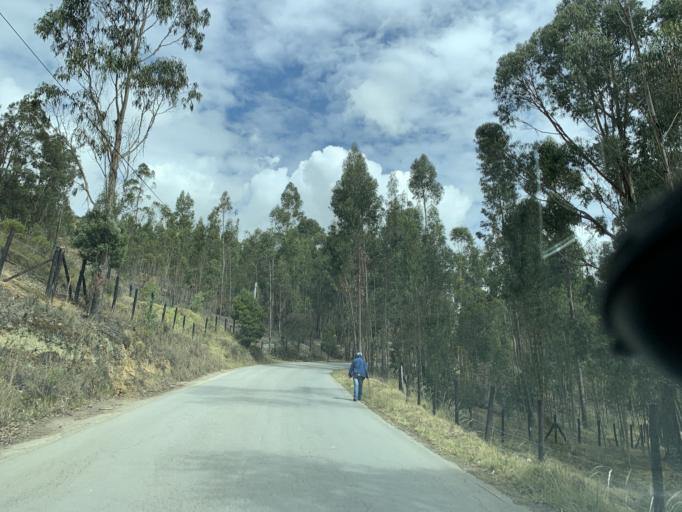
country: CO
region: Boyaca
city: Siachoque
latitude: 5.5701
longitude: -73.2669
